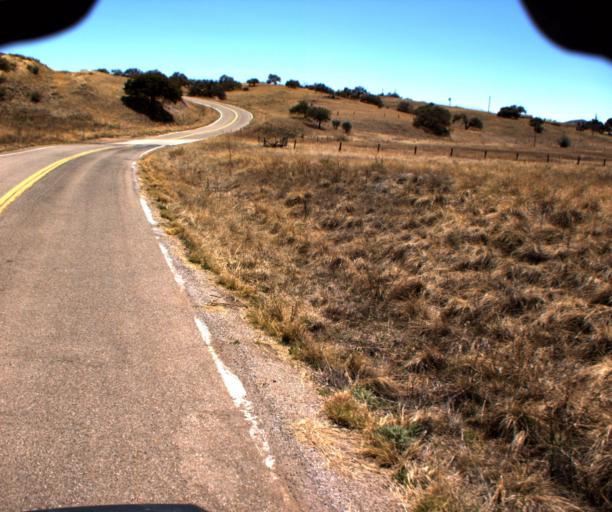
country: US
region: Arizona
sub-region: Cochise County
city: Huachuca City
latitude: 31.6068
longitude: -110.5786
